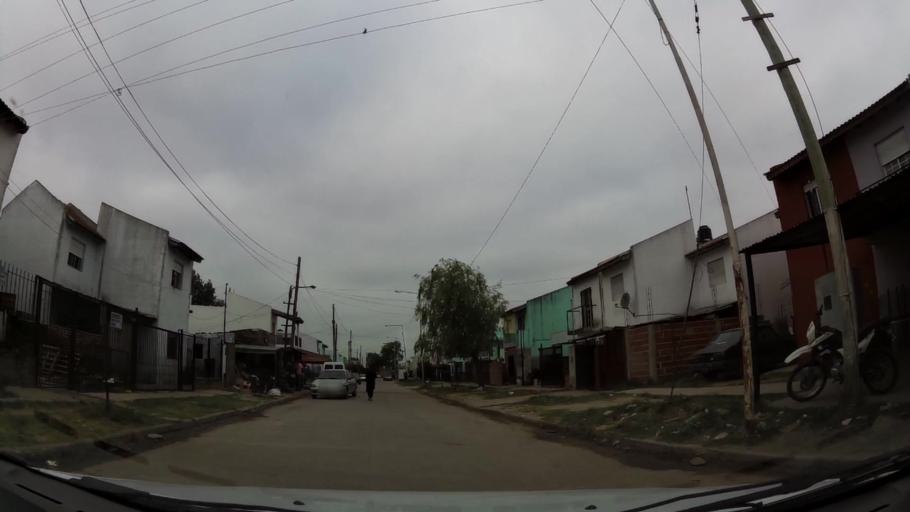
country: AR
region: Buenos Aires
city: San Justo
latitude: -34.6980
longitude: -58.5499
